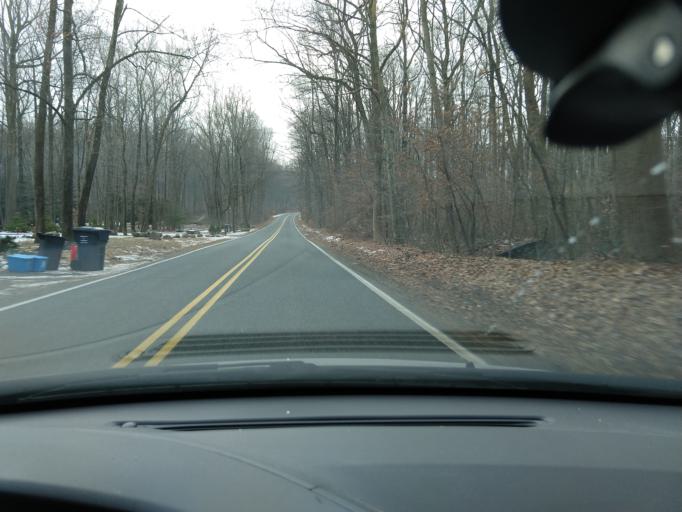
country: US
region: Pennsylvania
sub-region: Berks County
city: Birdsboro
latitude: 40.2352
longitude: -75.7724
